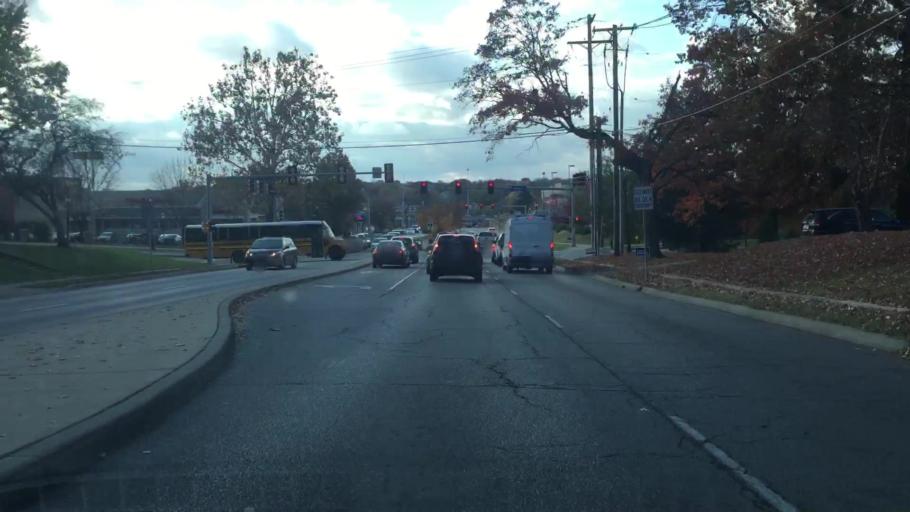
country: US
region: Kansas
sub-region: Johnson County
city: Merriam
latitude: 39.0223
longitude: -94.6856
